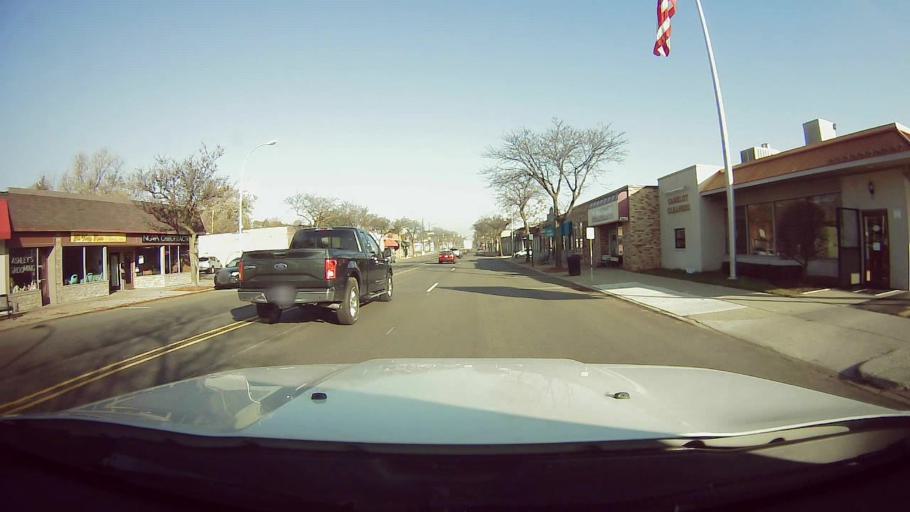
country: US
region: Michigan
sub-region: Oakland County
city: Berkley
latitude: 42.4972
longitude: -83.1836
